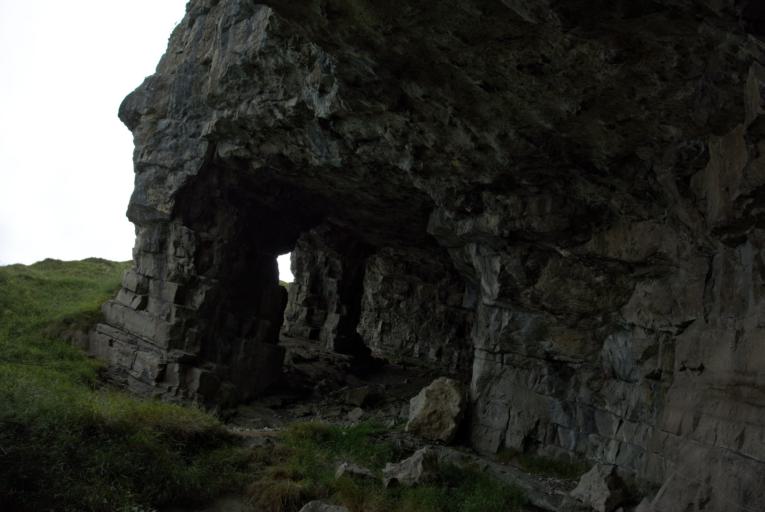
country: GB
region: Wales
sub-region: Conwy
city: Llandudno
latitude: 53.3321
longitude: -3.8313
